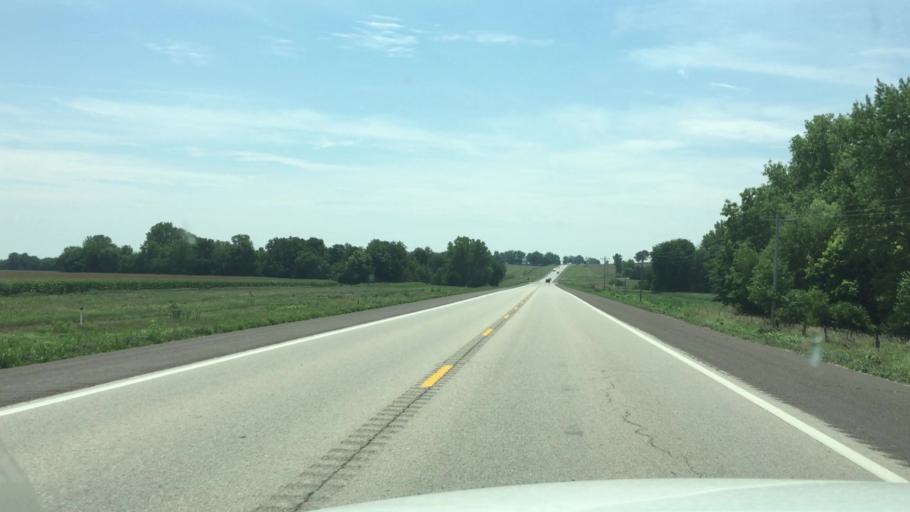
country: US
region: Kansas
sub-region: Jackson County
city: Holton
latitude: 39.5796
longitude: -95.7323
